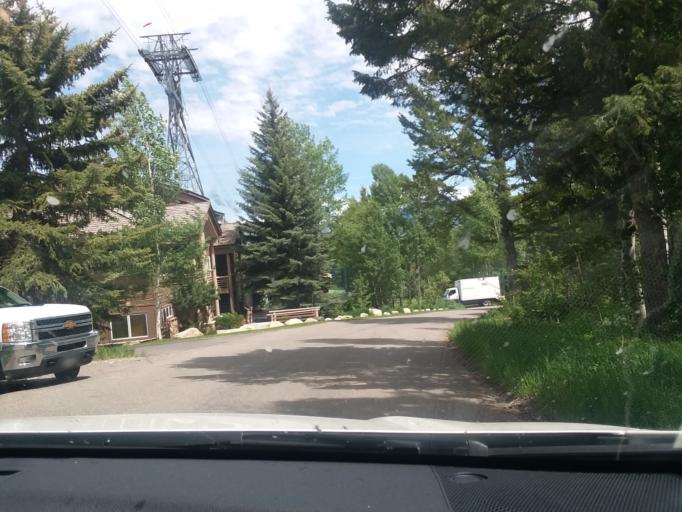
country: US
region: Wyoming
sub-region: Teton County
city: Moose Wilson Road
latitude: 43.5884
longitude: -110.8329
